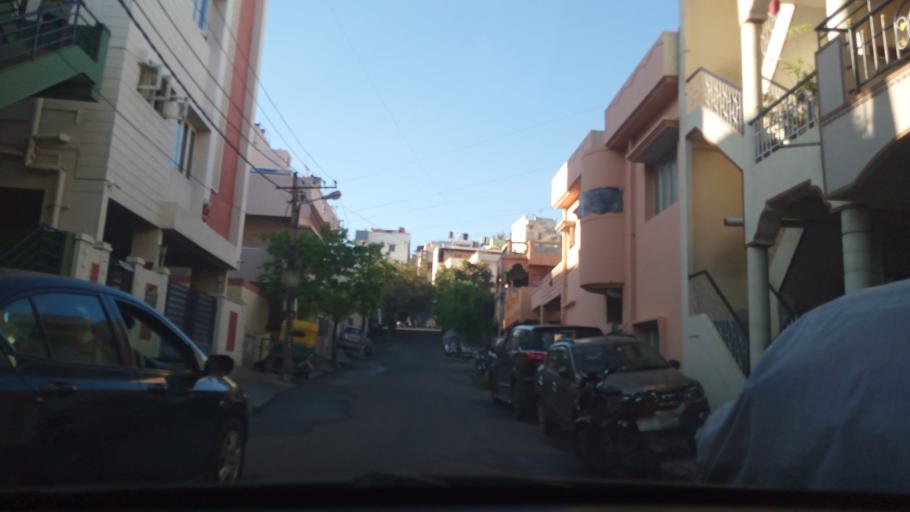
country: IN
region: Karnataka
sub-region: Bangalore Urban
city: Bangalore
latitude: 13.0116
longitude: 77.5431
